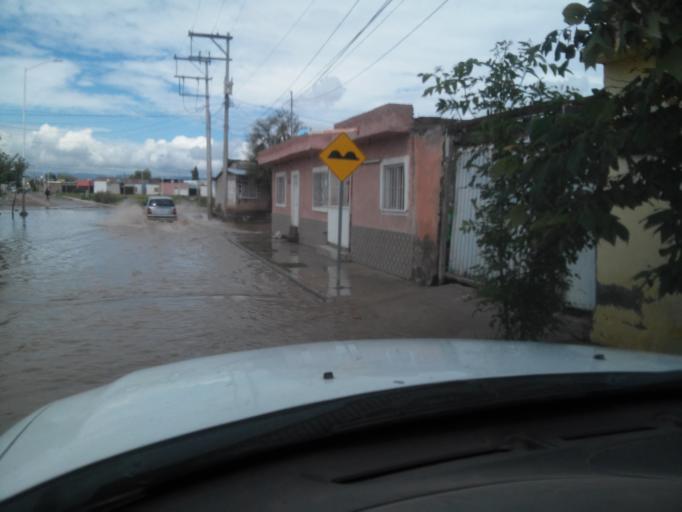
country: MX
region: Durango
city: Victoria de Durango
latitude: 24.0175
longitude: -104.6082
